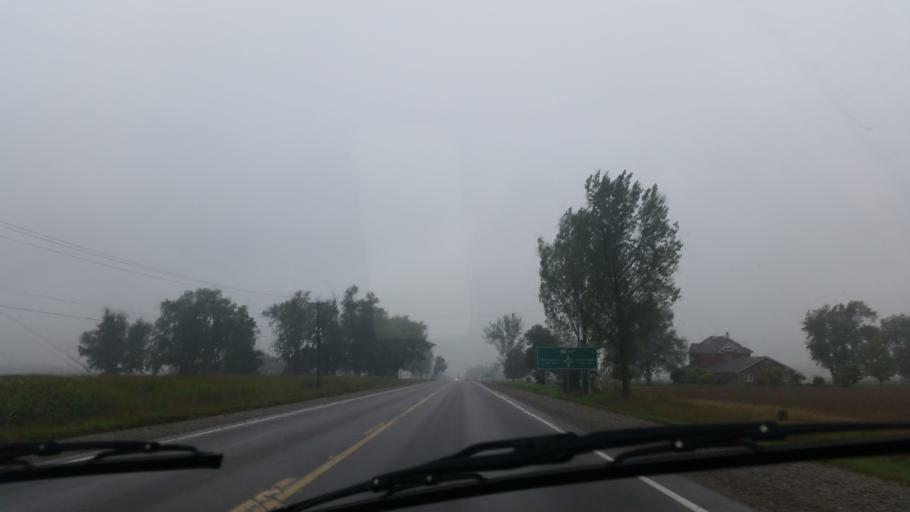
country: CA
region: Ontario
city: Stratford
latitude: 43.3284
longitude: -81.0191
